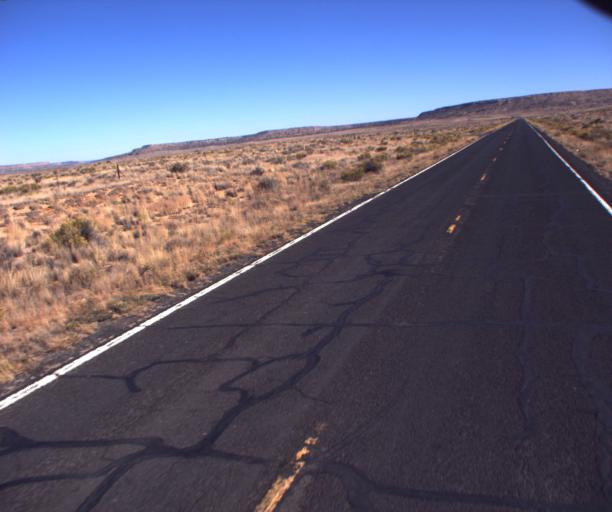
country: US
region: Arizona
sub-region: Navajo County
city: First Mesa
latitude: 35.8409
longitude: -110.3414
